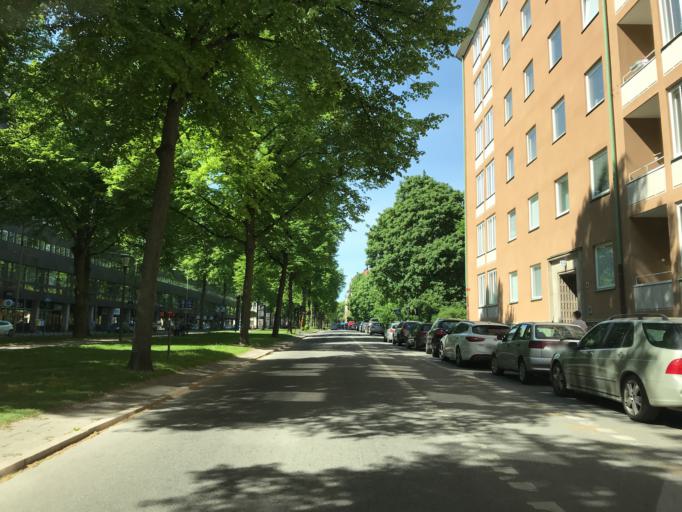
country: SE
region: Stockholm
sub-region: Stockholms Kommun
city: OEstermalm
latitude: 59.3360
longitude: 18.0987
